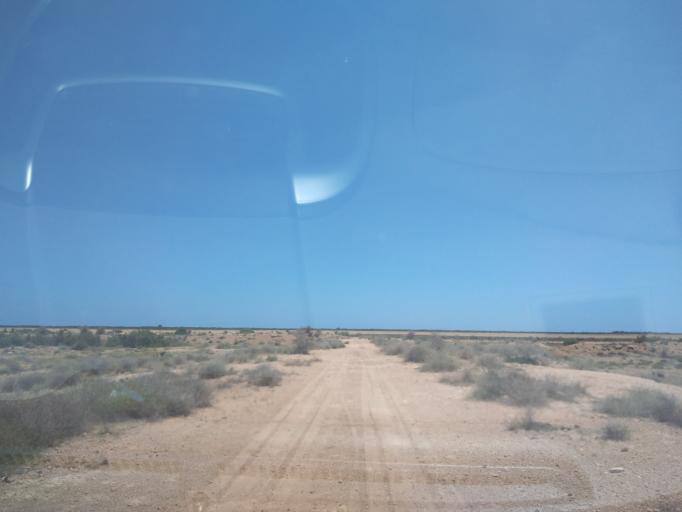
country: TN
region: Susah
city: Harqalah
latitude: 36.1702
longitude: 10.4466
